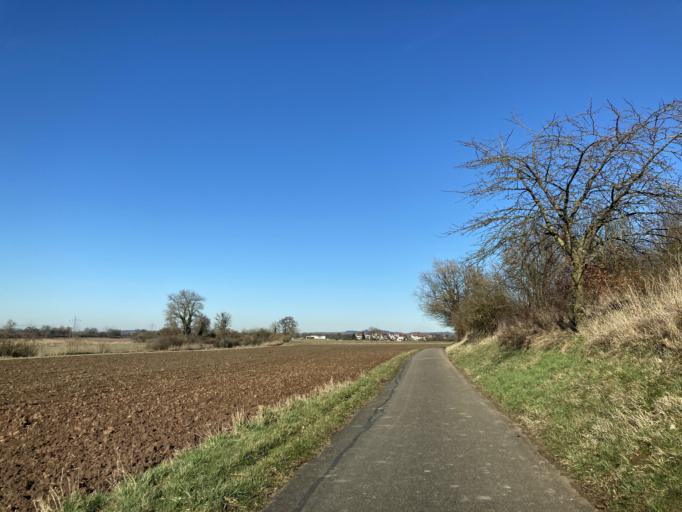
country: DE
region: Baden-Wuerttemberg
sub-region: Freiburg Region
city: Eichstetten
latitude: 48.0964
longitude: 7.7673
